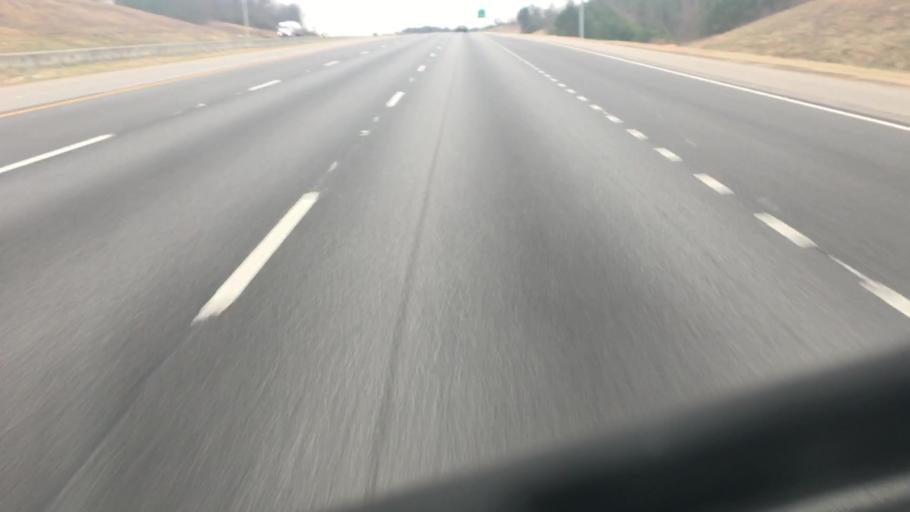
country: US
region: Alabama
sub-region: Jefferson County
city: Fultondale
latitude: 33.5814
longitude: -86.8262
